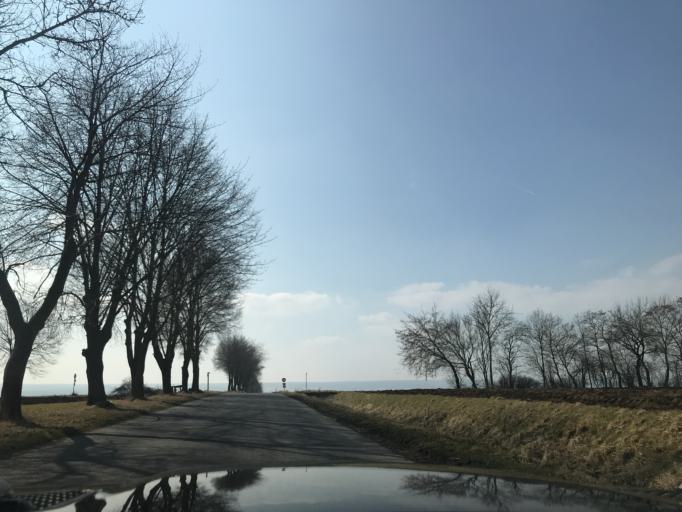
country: DE
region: Thuringia
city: Heroldishausen
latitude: 51.1414
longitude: 10.5086
